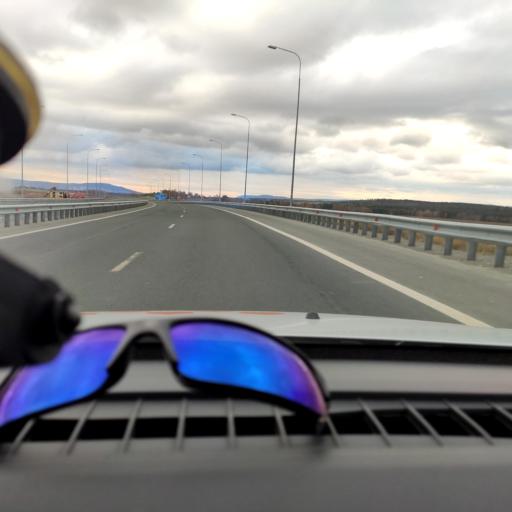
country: RU
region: Samara
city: Bereza
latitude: 53.4990
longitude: 50.1164
